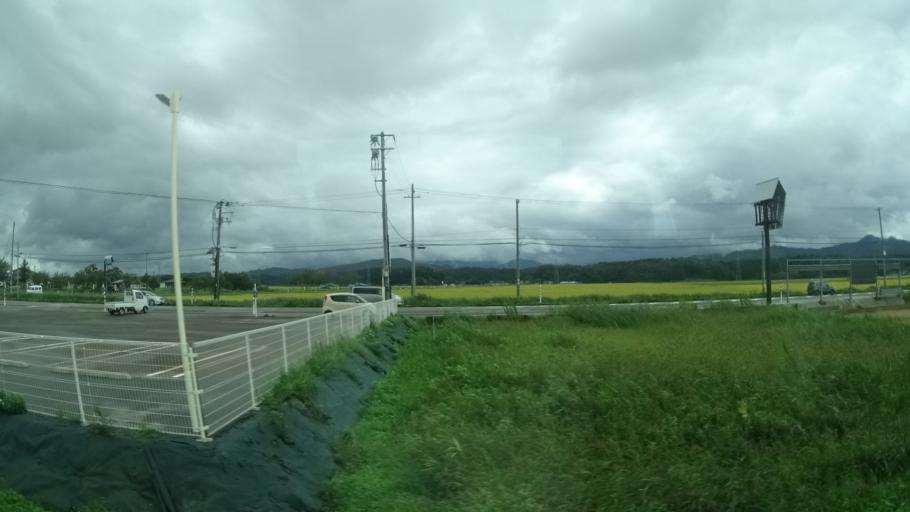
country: JP
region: Niigata
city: Murakami
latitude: 38.1709
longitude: 139.4595
